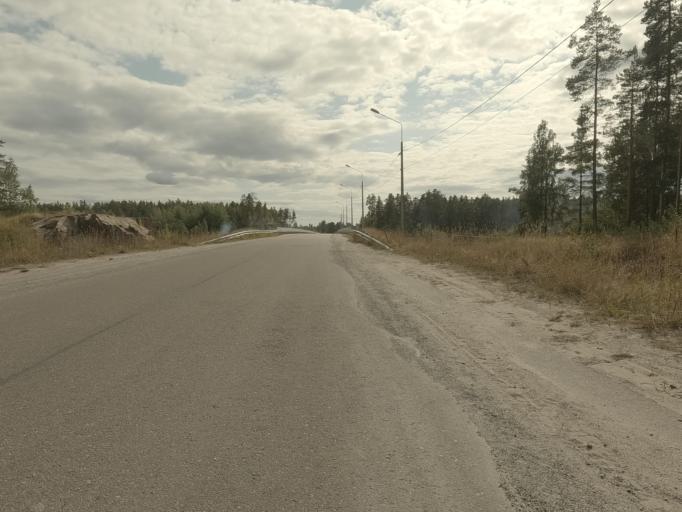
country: RU
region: Leningrad
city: Kamennogorsk
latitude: 60.9604
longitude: 29.1403
